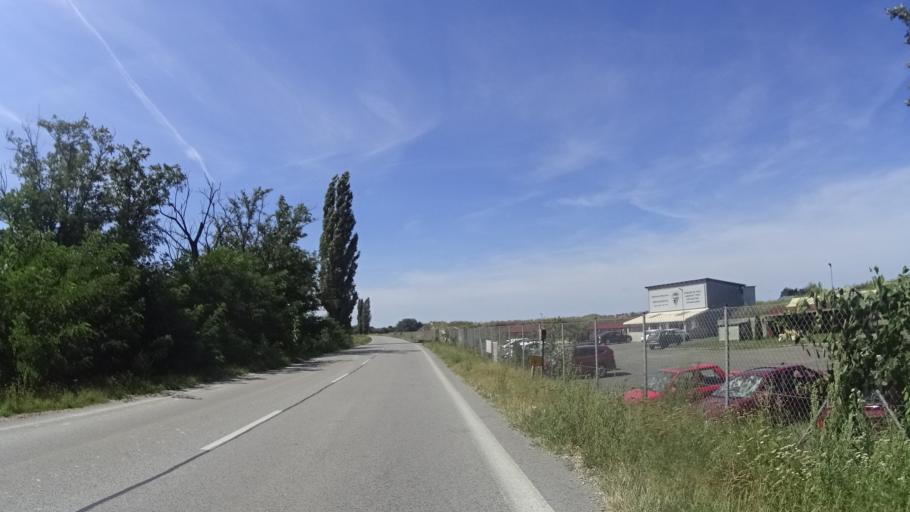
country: AT
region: Lower Austria
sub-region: Politischer Bezirk Ganserndorf
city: Marchegg
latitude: 48.3055
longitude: 16.9625
